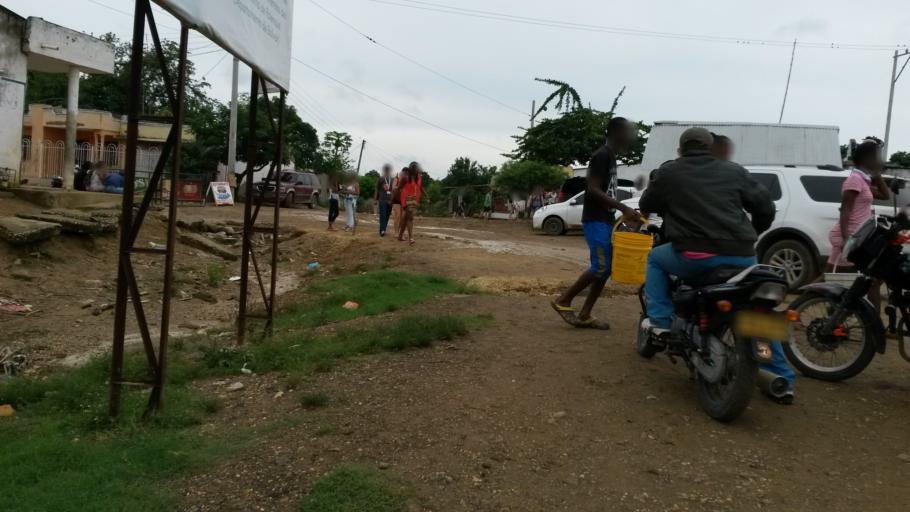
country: CO
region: Bolivar
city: San Pablo
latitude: 10.1060
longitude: -75.2007
